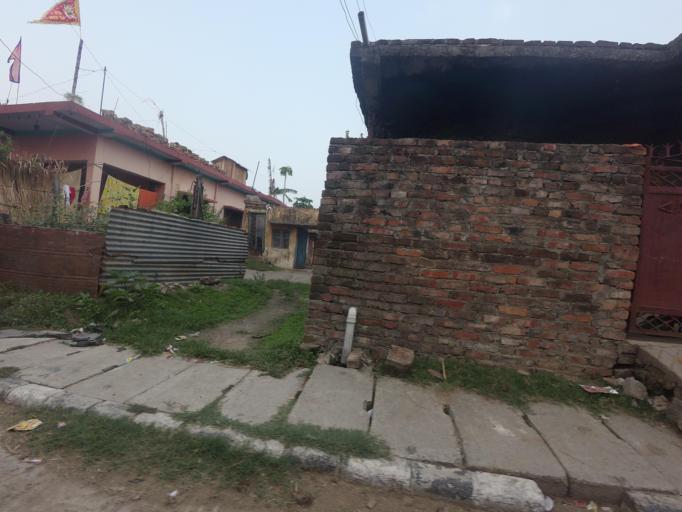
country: NP
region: Western Region
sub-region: Lumbini Zone
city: Bhairahawa
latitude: 27.5103
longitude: 83.4246
